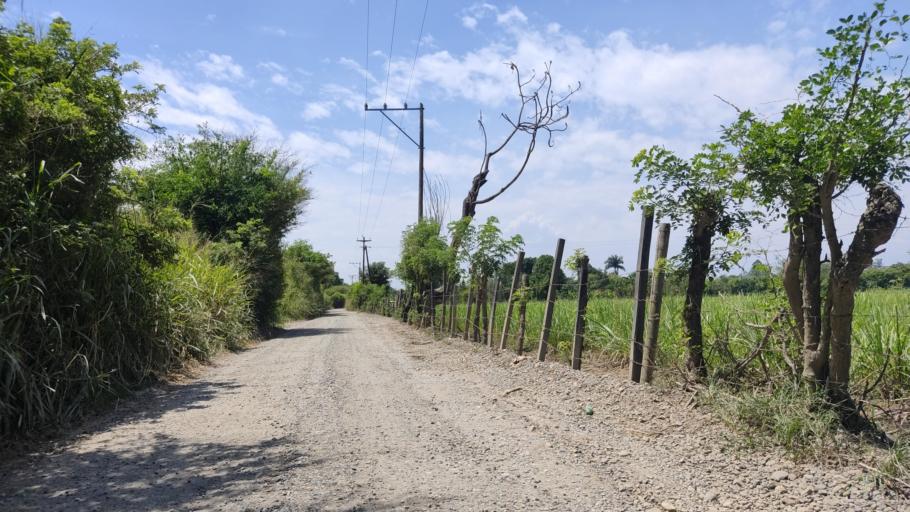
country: CO
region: Valle del Cauca
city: Jamundi
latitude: 3.1631
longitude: -76.5089
